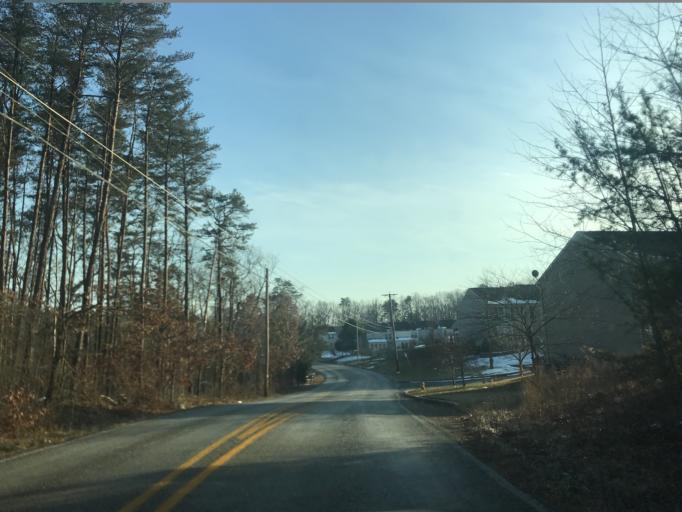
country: US
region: Maryland
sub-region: Harford County
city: Joppatowne
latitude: 39.4152
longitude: -76.3461
